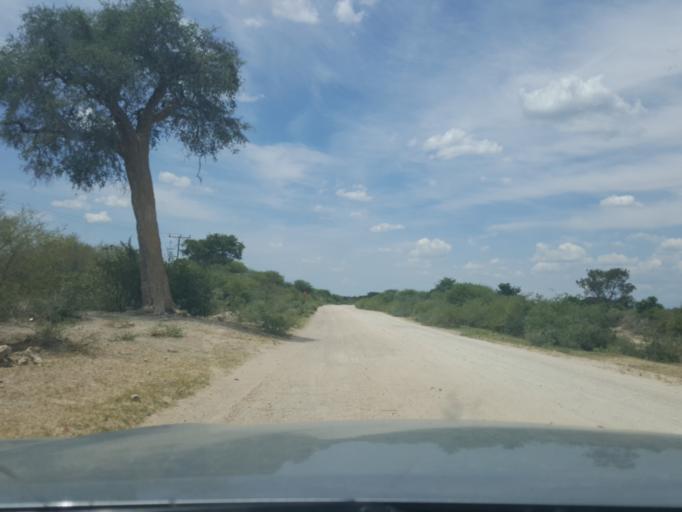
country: BW
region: North West
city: Shakawe
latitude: -18.3177
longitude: 21.9064
